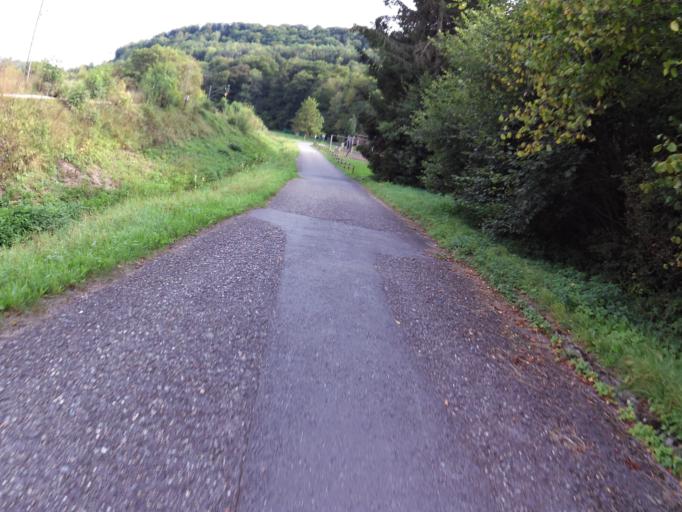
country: DE
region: Baden-Wuerttemberg
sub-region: Freiburg Region
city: Villingendorf
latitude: 48.2212
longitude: 8.5989
